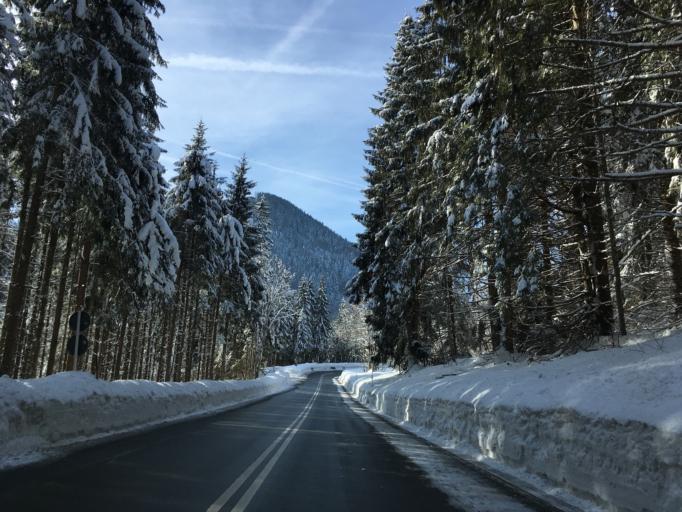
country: DE
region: Bavaria
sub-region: Upper Bavaria
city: Burg Unter-Falkenstein
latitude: 47.6710
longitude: 12.0758
